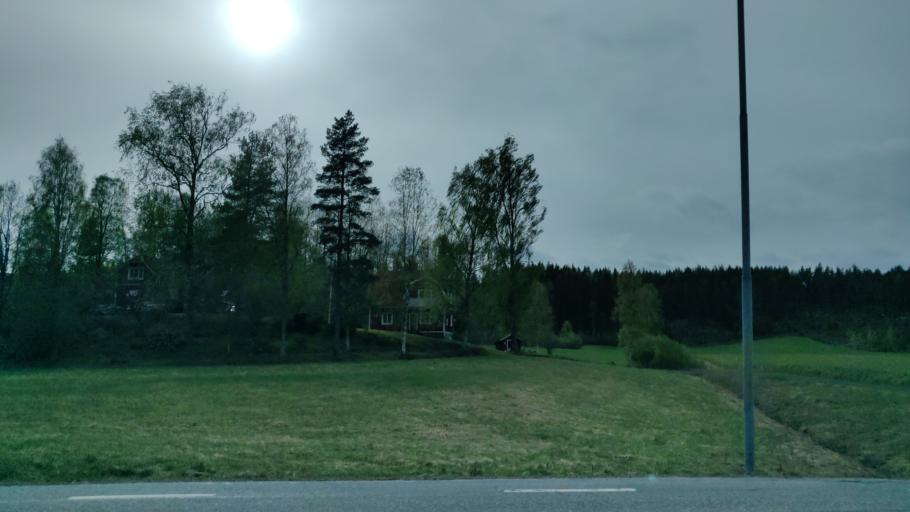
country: SE
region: Vaermland
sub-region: Munkfors Kommun
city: Munkfors
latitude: 59.8112
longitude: 13.5072
